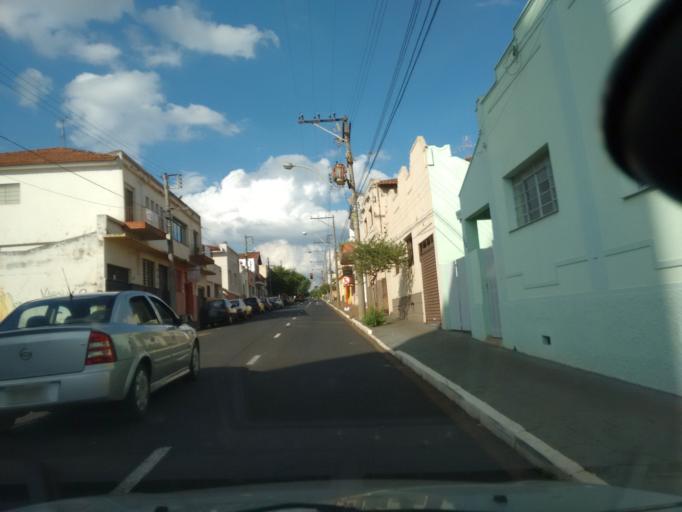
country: BR
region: Sao Paulo
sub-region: Araraquara
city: Araraquara
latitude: -21.7925
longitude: -48.1677
